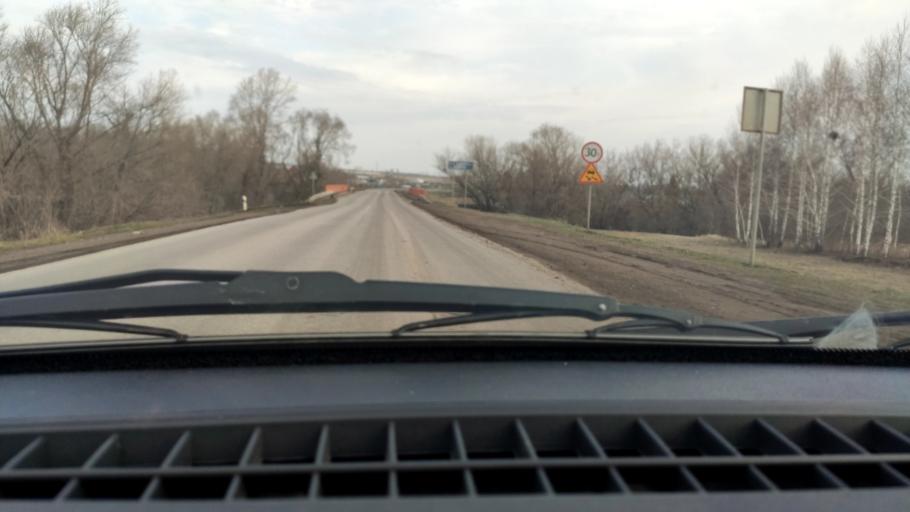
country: RU
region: Bashkortostan
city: Davlekanovo
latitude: 54.3643
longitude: 55.1958
